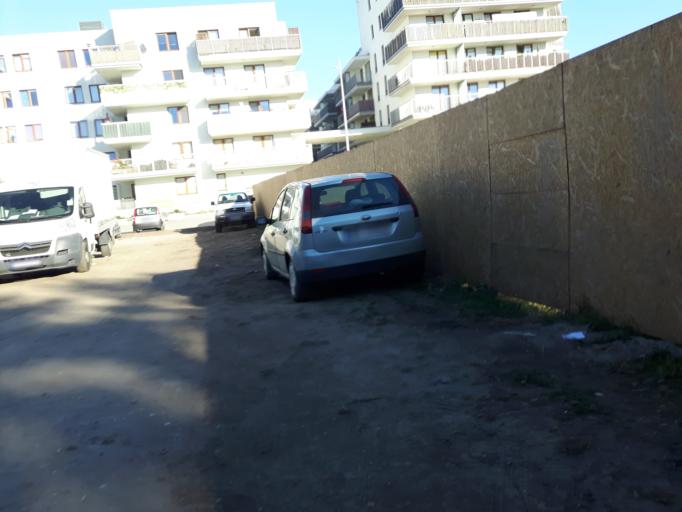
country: PL
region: Masovian Voivodeship
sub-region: Powiat wolominski
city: Zabki
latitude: 52.2806
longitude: 21.1333
